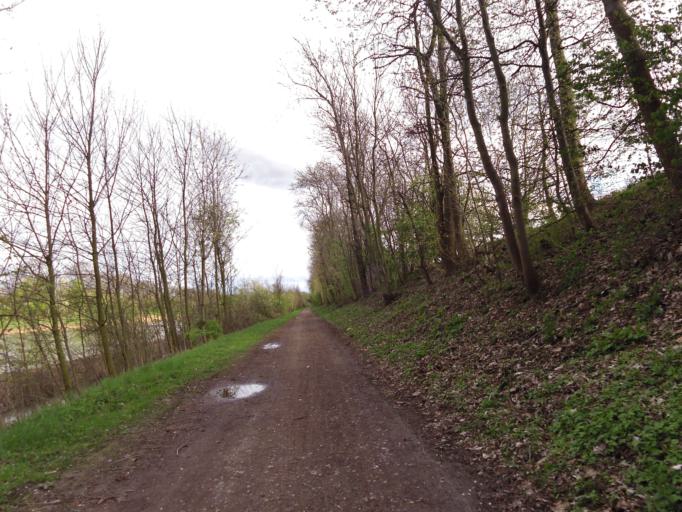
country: DE
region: Lower Saxony
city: Laatzen
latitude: 52.3734
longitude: 9.8498
